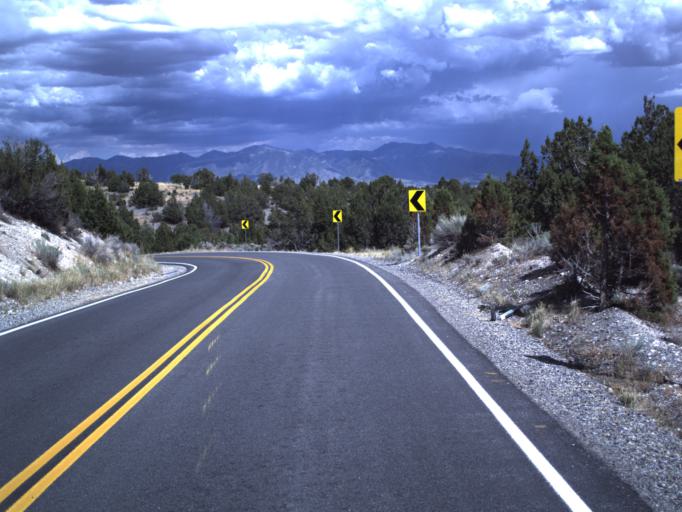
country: US
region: Utah
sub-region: Tooele County
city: Grantsville
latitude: 40.3483
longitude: -112.5530
